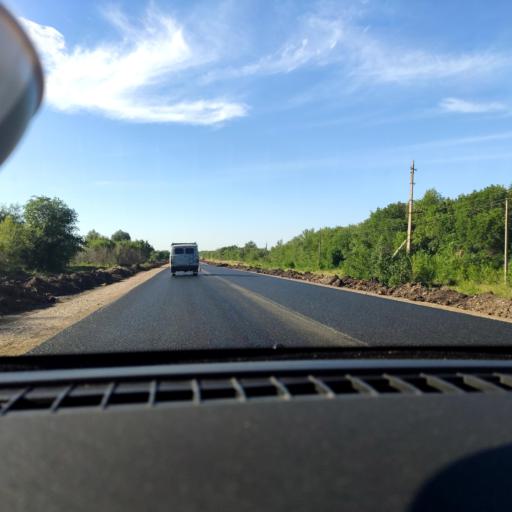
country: RU
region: Samara
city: Krasnoarmeyskoye
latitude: 52.8131
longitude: 50.0112
